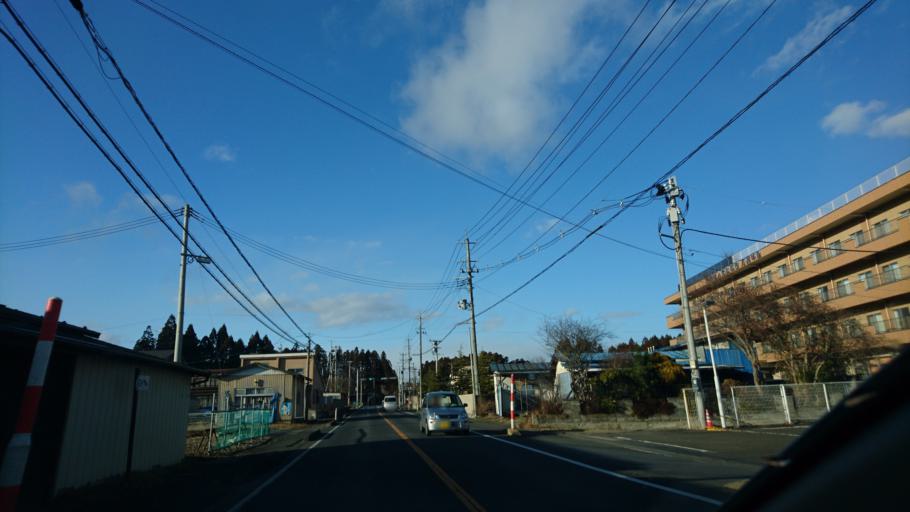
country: JP
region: Miyagi
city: Tomiya
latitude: 38.4659
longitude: 140.8694
